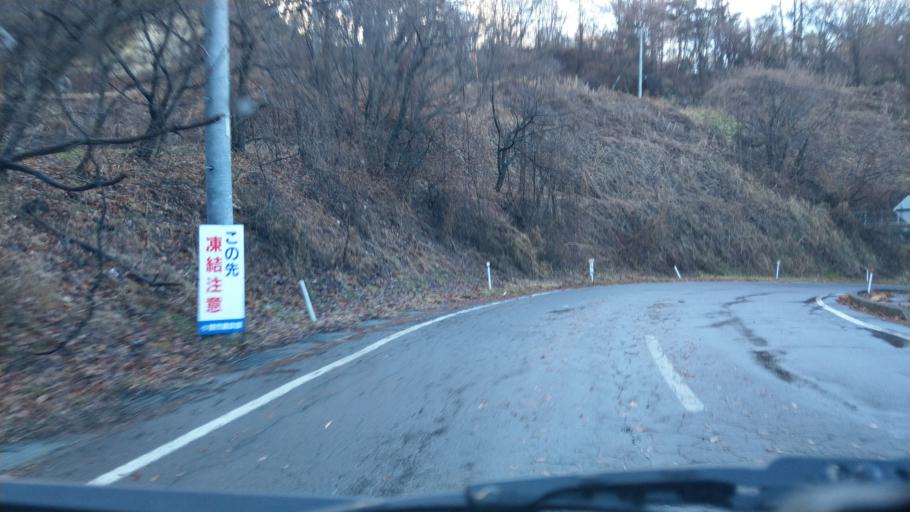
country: JP
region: Nagano
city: Komoro
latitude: 36.2988
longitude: 138.4139
